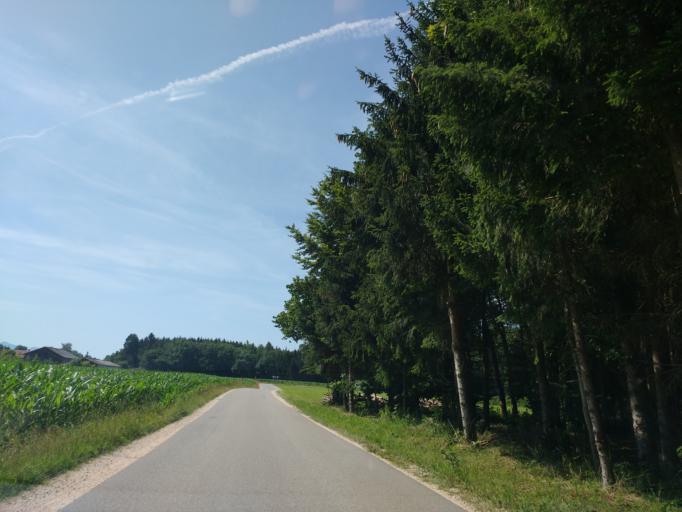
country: DE
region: Bavaria
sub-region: Upper Bavaria
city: Seeon-Seebruck
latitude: 47.9926
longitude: 12.4486
